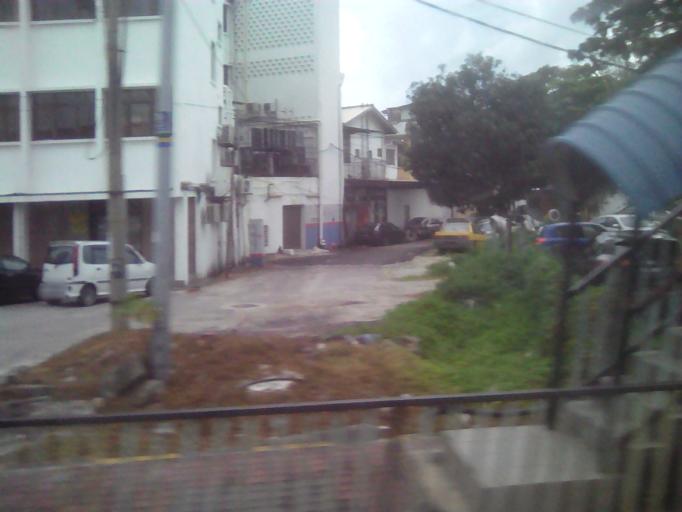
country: MY
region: Penang
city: Butterworth
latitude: 5.3971
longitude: 100.3681
